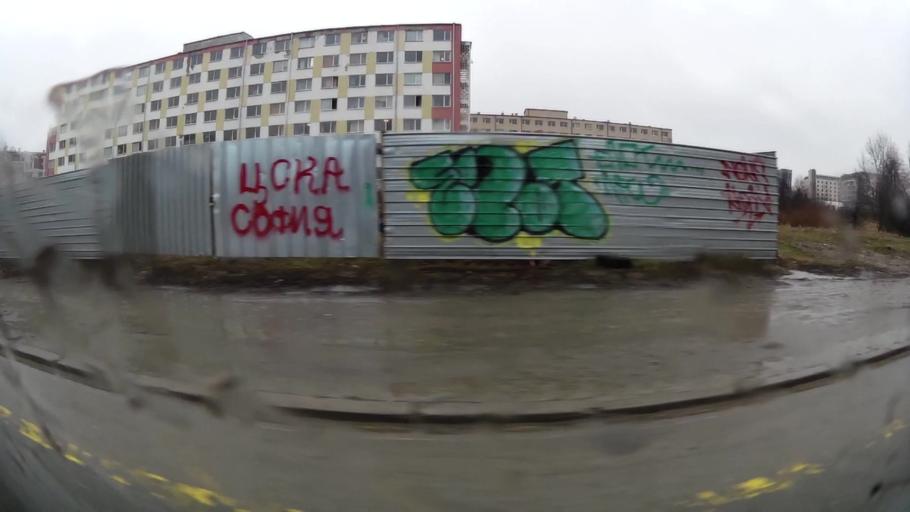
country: BG
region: Sofia-Capital
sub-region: Stolichna Obshtina
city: Sofia
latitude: 42.6582
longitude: 23.3487
